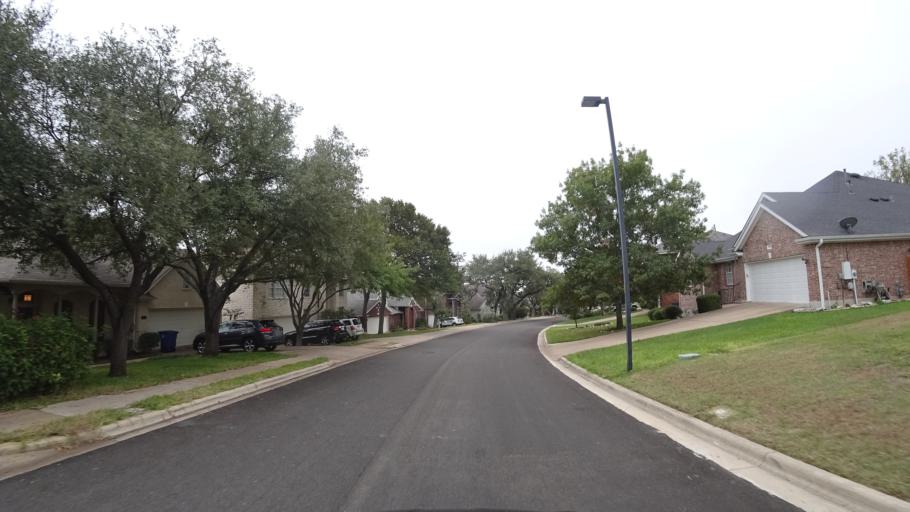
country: US
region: Texas
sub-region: Travis County
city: Shady Hollow
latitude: 30.1846
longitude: -97.8907
